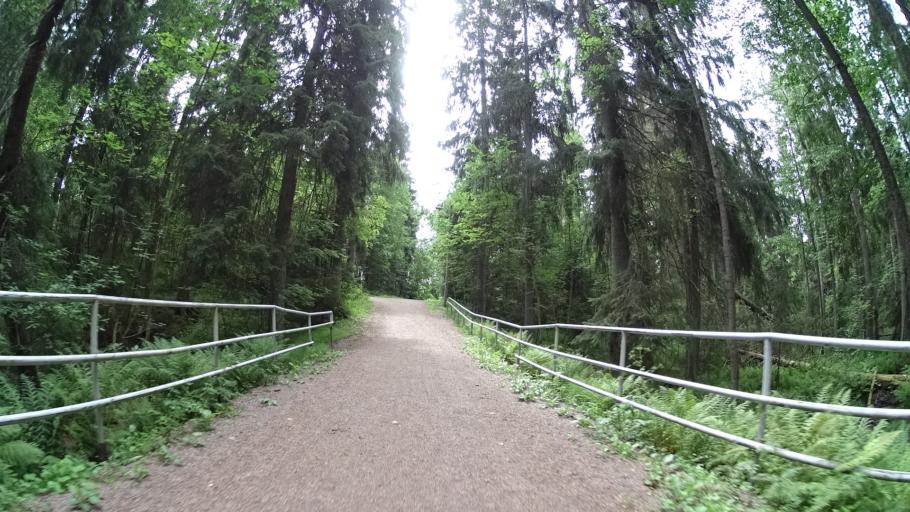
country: FI
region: Uusimaa
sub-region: Helsinki
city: Kilo
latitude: 60.2885
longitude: 24.7474
